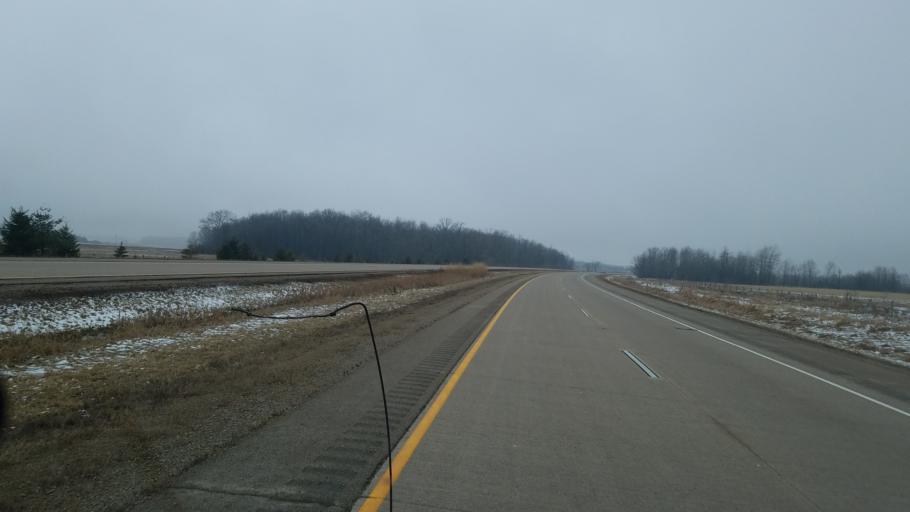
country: US
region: Wisconsin
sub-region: Winnebago County
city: Winneconne
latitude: 44.2351
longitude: -88.7767
